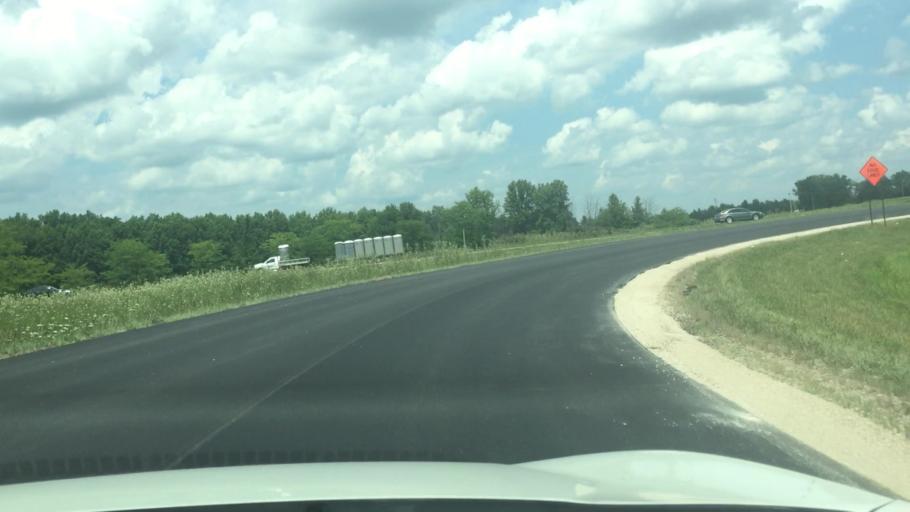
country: US
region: Ohio
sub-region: Champaign County
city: North Lewisburg
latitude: 40.2678
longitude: -83.5012
